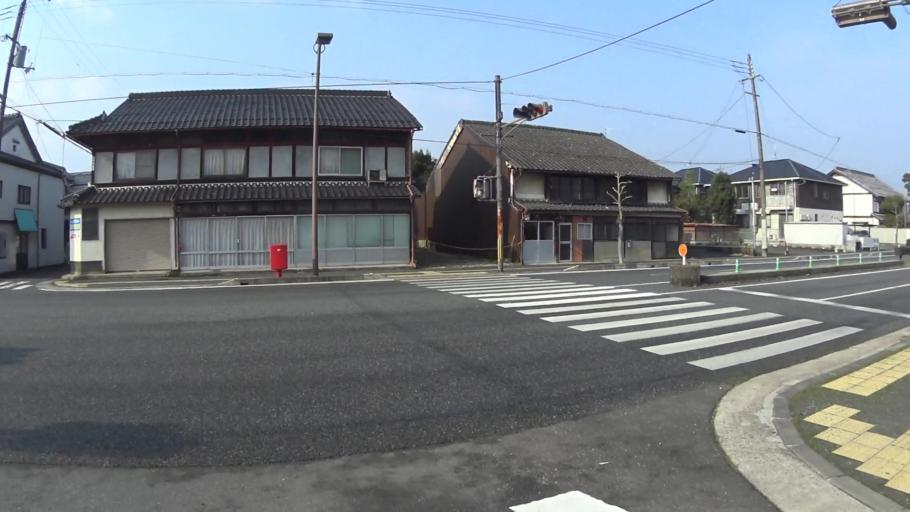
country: JP
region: Kyoto
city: Fukuchiyama
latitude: 35.3003
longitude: 135.1283
